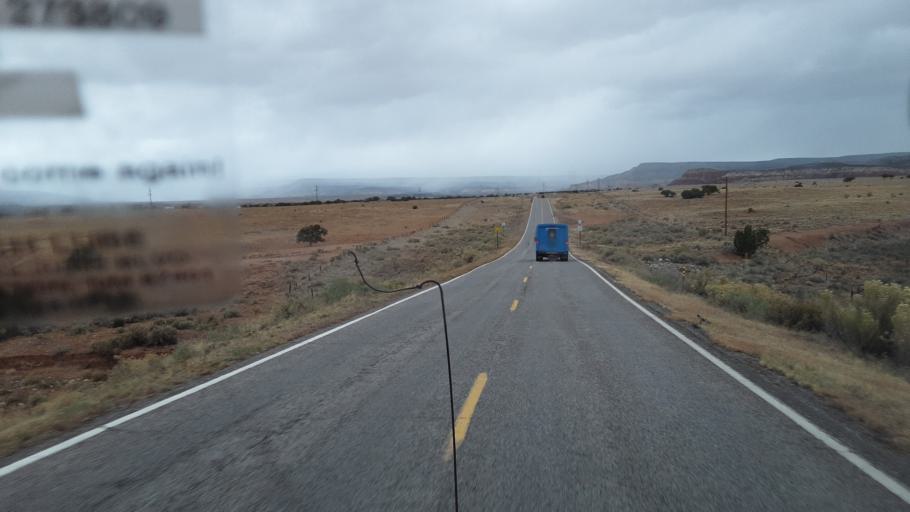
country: US
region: New Mexico
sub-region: Rio Arriba County
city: Santa Teresa
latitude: 36.2613
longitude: -106.4178
